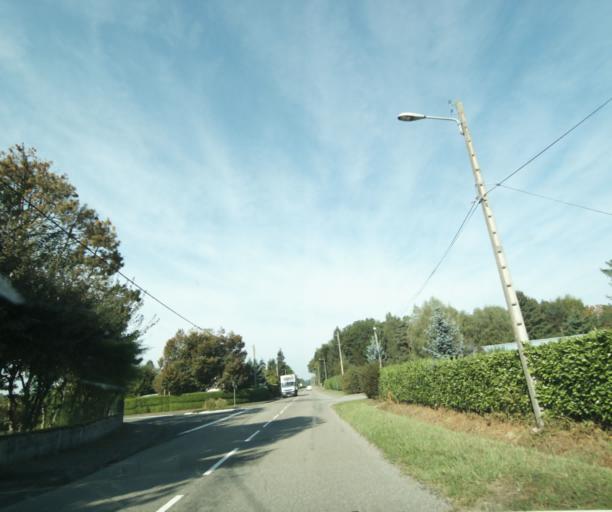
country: FR
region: Bourgogne
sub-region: Departement de Saone-et-Loire
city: Genelard
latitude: 46.5759
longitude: 4.2527
